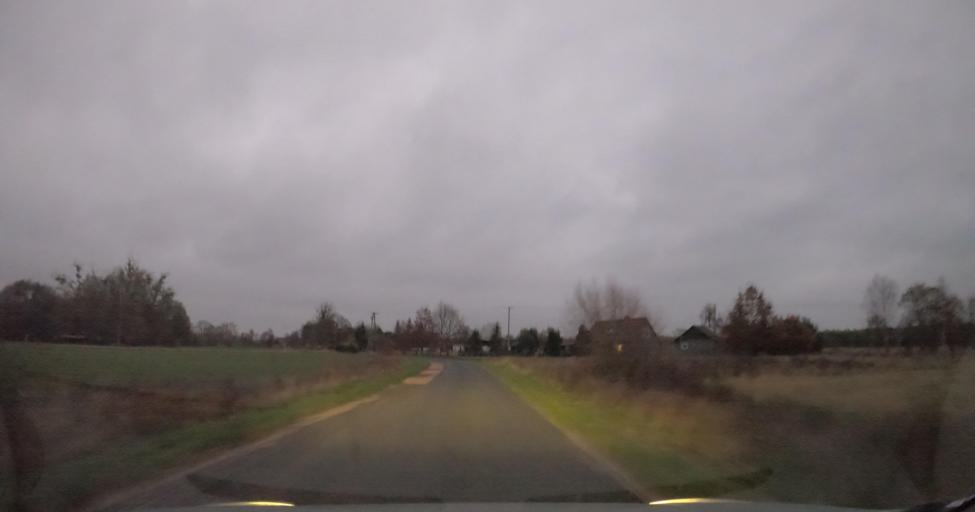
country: PL
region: West Pomeranian Voivodeship
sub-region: Powiat bialogardzki
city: Tychowo
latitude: 53.8708
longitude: 16.2341
